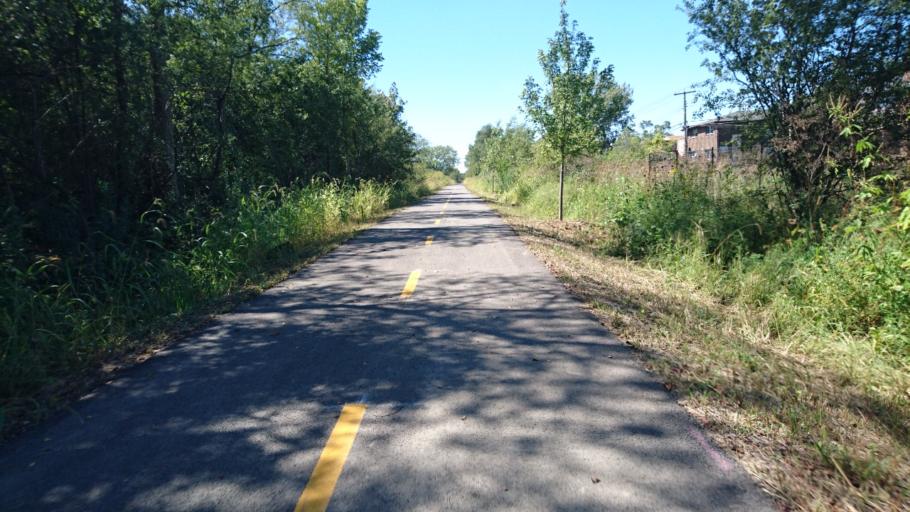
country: US
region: Illinois
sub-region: Cook County
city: Park Forest
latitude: 41.4990
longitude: -87.6603
